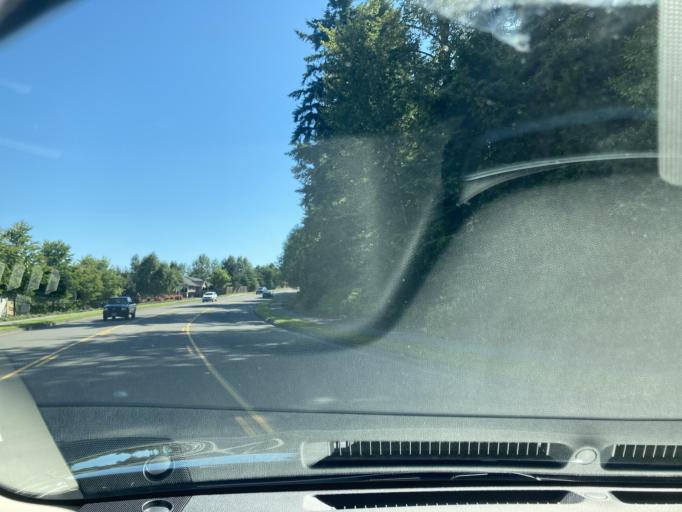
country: US
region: Washington
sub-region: Pierce County
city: Graham
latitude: 47.0858
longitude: -122.3019
